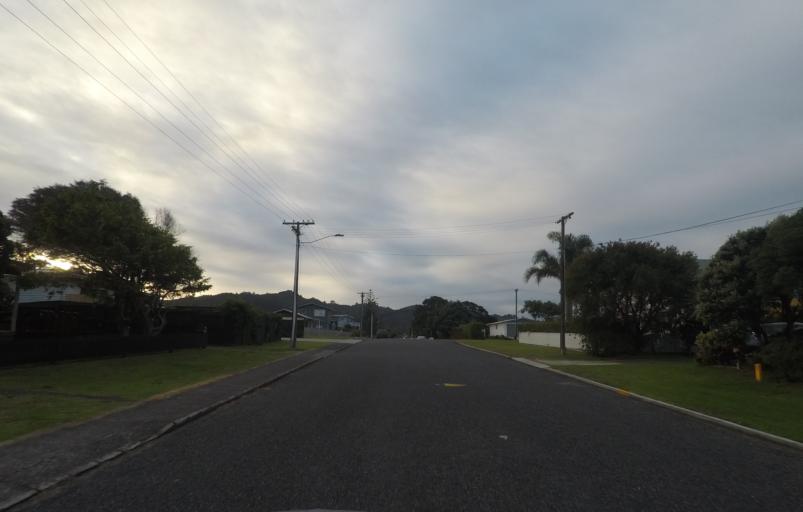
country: NZ
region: Bay of Plenty
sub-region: Western Bay of Plenty District
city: Waihi Beach
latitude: -37.4093
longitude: 175.9423
